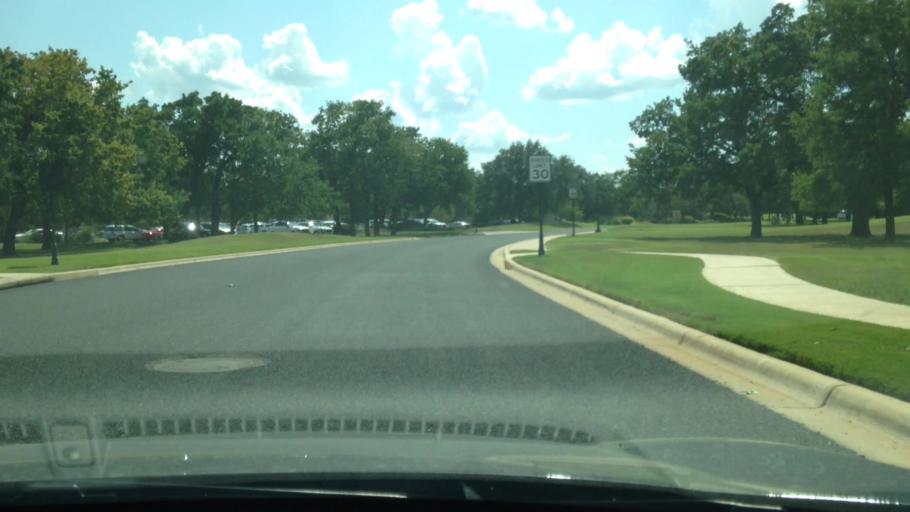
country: US
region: Texas
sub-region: Williamson County
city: Leander
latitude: 30.6403
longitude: -97.7933
